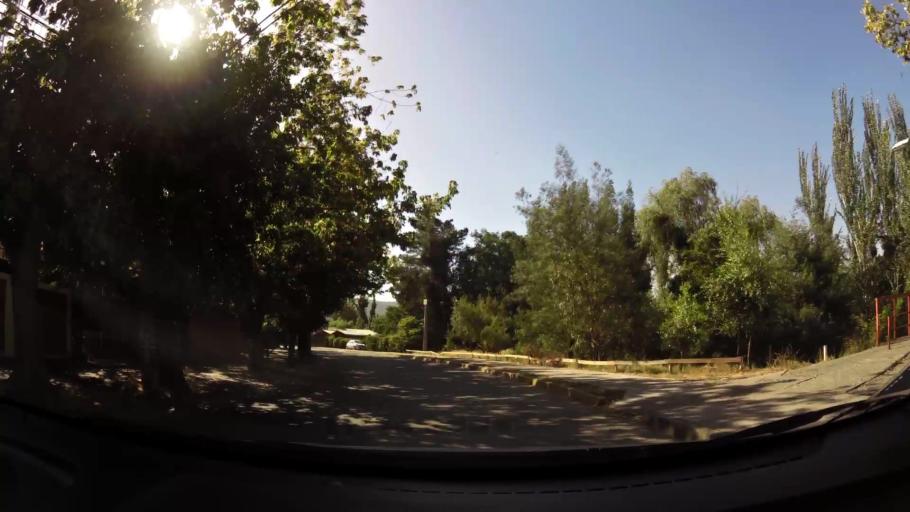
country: CL
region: Maule
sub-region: Provincia de Talca
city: Talca
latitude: -35.4269
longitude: -71.6709
